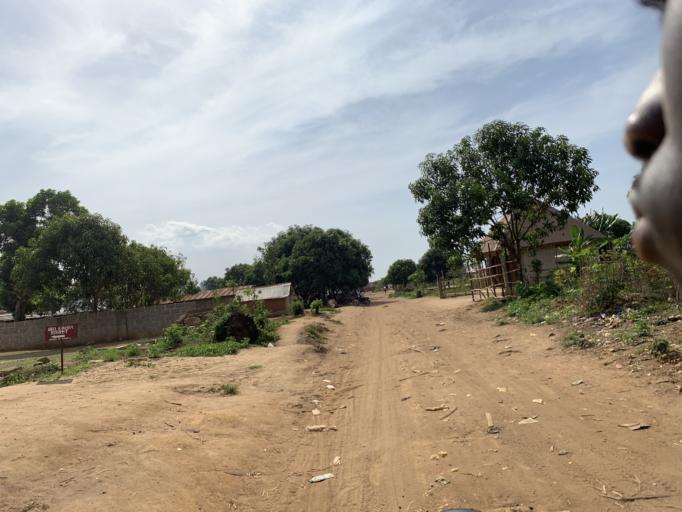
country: SL
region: Western Area
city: Waterloo
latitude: 8.3451
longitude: -13.0500
